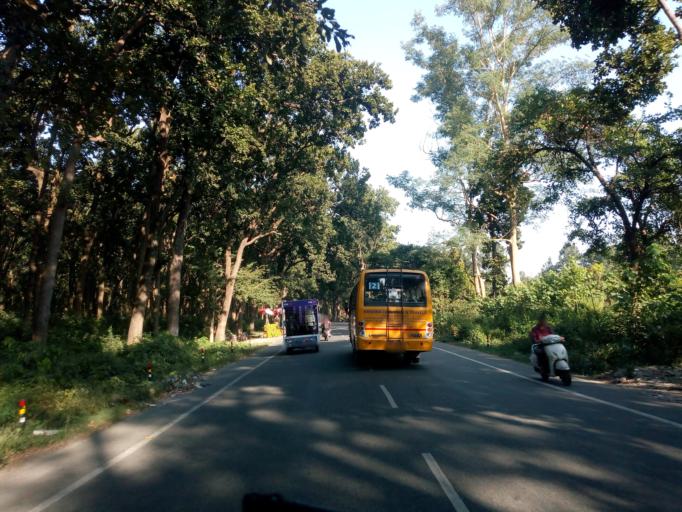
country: IN
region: Uttarakhand
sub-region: Dehradun
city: Dehradun
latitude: 30.3471
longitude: 77.8795
